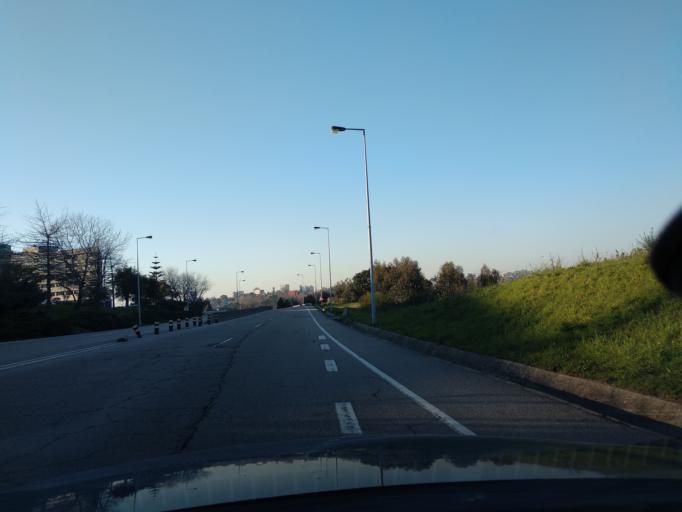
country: PT
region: Porto
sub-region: Vila Nova de Gaia
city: Vila Nova de Gaia
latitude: 41.1415
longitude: -8.6347
